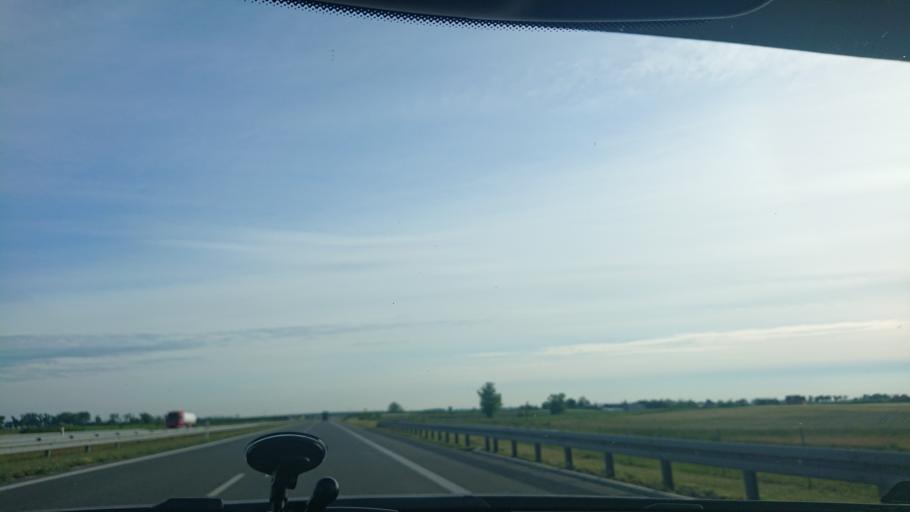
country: PL
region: Greater Poland Voivodeship
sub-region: Powiat gnieznienski
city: Gniezno
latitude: 52.5441
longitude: 17.5298
